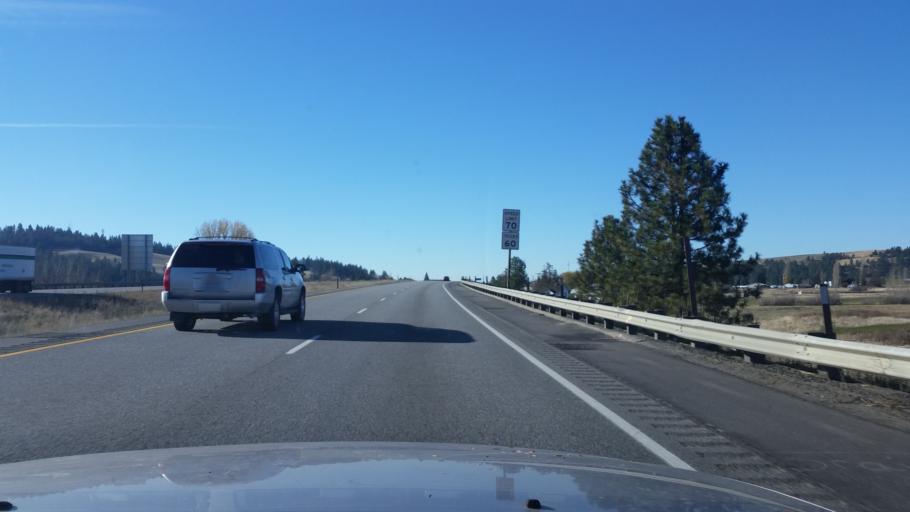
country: US
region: Washington
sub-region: Spokane County
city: Fairchild Air Force Base
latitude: 47.5641
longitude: -117.5971
